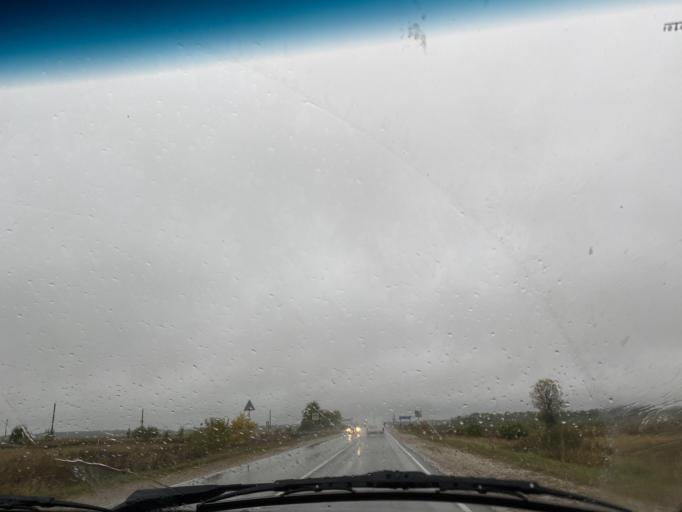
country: RU
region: Rjazan
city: Ryazan'
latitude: 54.4857
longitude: 39.8234
